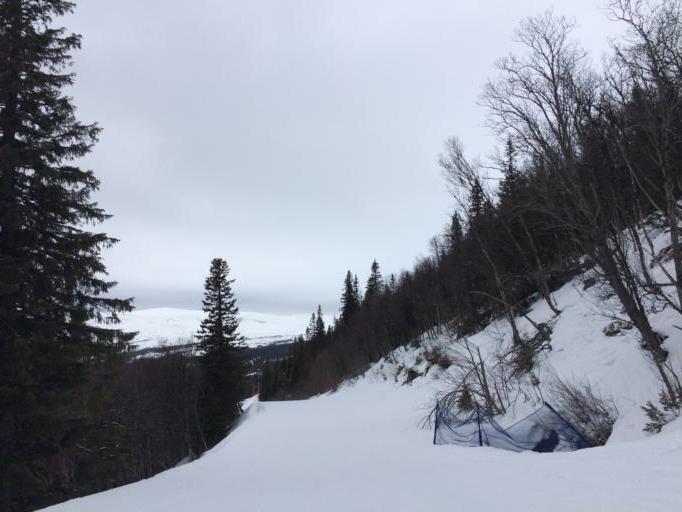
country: SE
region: Jaemtland
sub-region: Are Kommun
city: Are
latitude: 63.4098
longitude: 13.0714
